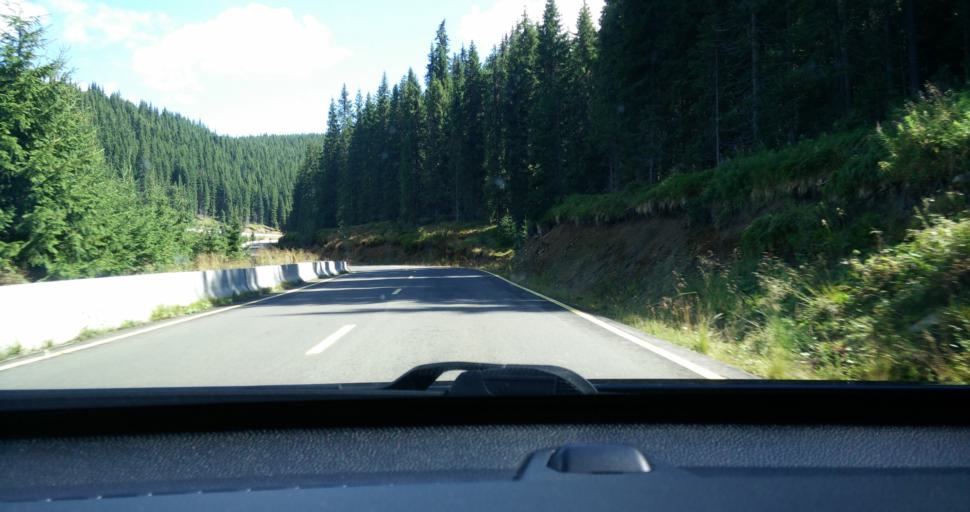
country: RO
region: Hunedoara
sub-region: Oras Petrila
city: Petrila
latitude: 45.4606
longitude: 23.6176
